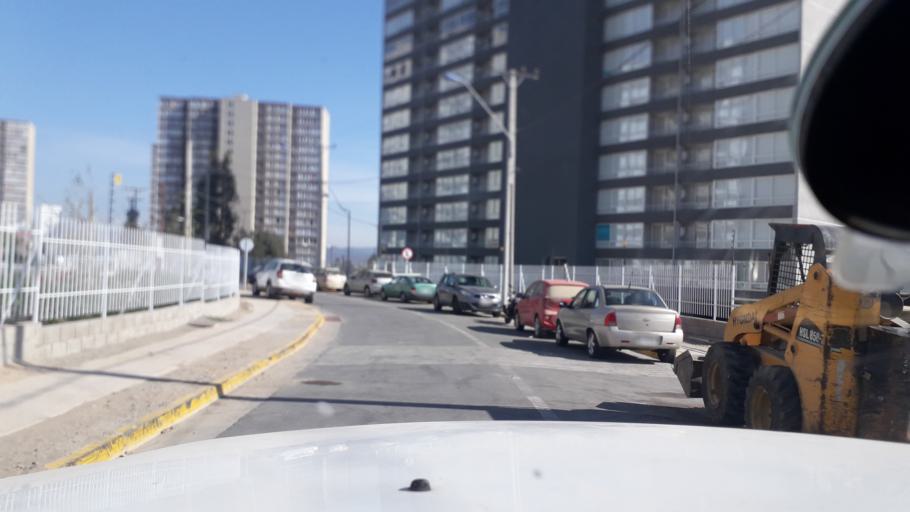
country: CL
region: Valparaiso
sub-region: Provincia de Marga Marga
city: Quilpue
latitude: -33.0667
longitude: -71.4125
